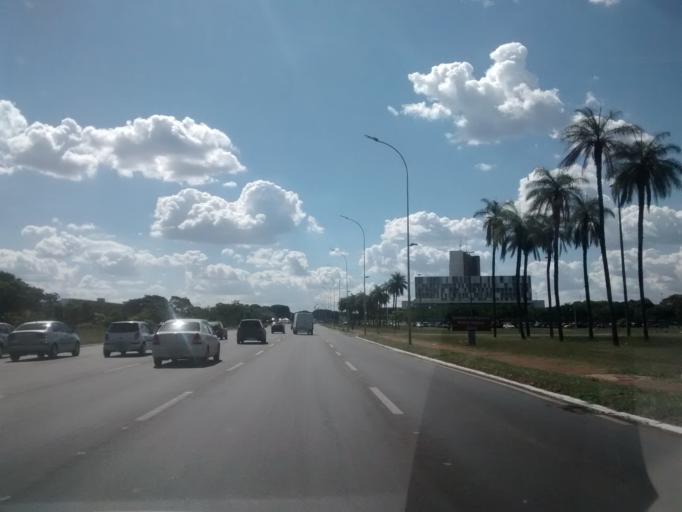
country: BR
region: Federal District
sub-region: Brasilia
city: Brasilia
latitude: -15.7855
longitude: -47.9031
